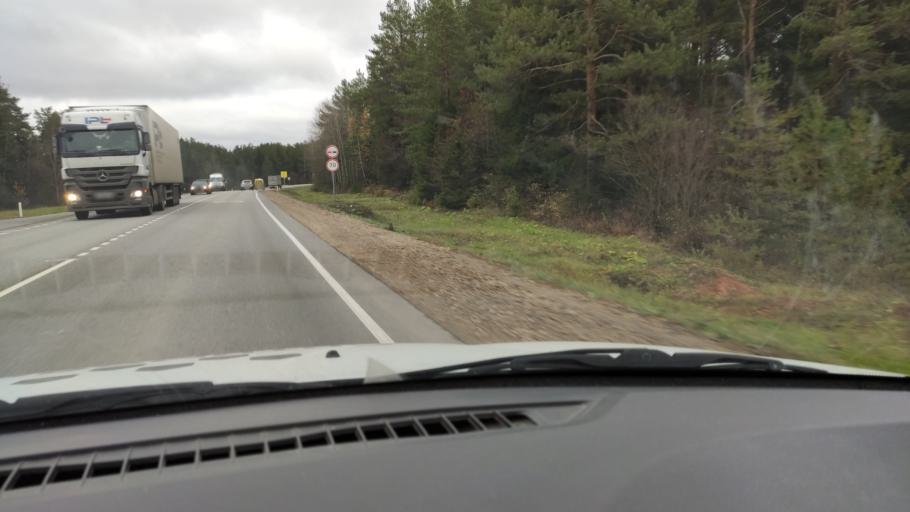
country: RU
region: Kirov
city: Slobodskoy
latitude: 58.7548
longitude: 50.3243
